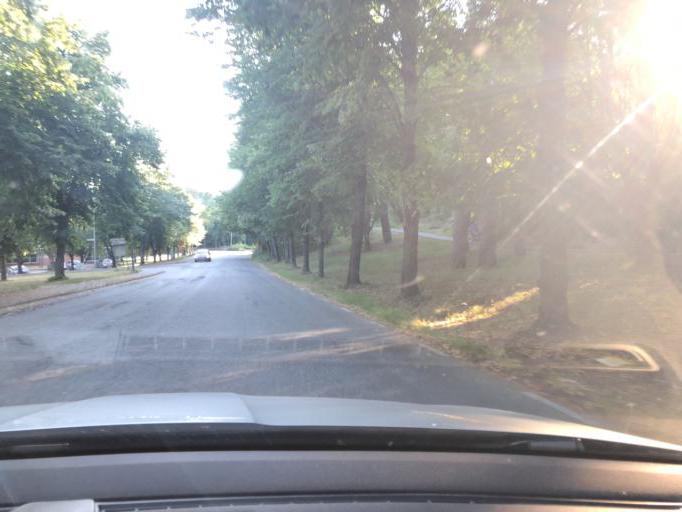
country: SE
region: Stockholm
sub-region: Sodertalje Kommun
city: Soedertaelje
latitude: 59.1808
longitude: 17.6225
